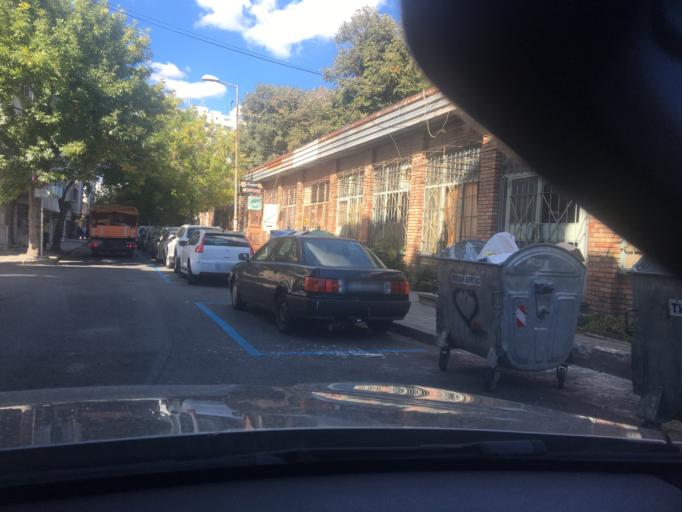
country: BG
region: Burgas
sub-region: Obshtina Burgas
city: Burgas
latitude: 42.4997
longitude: 27.4749
